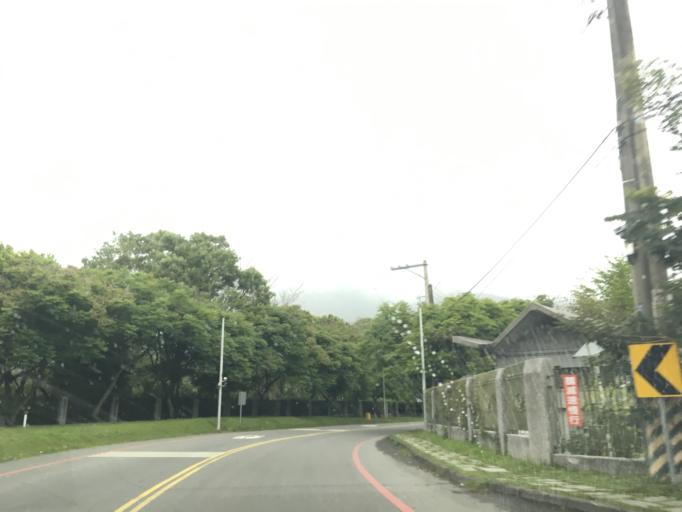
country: TW
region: Taiwan
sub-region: Hualien
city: Hualian
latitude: 23.9973
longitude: 121.5743
